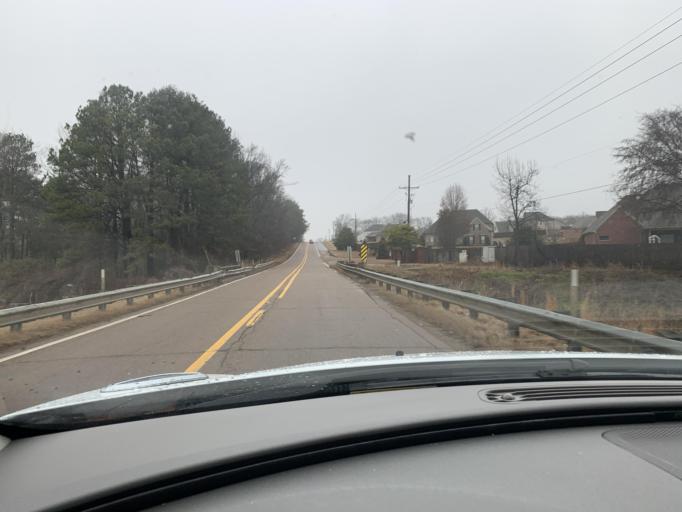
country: US
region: Mississippi
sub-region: De Soto County
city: Hernando
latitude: 34.8514
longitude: -89.9951
